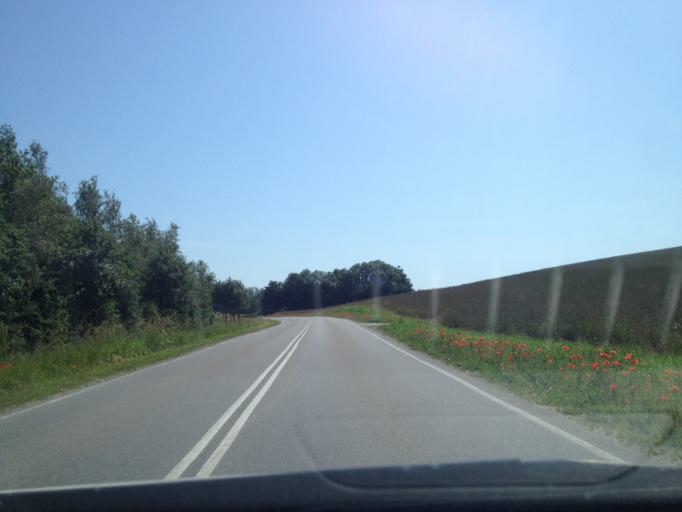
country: DK
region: Central Jutland
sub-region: Samso Kommune
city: Tranebjerg
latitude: 55.8577
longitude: 10.5718
